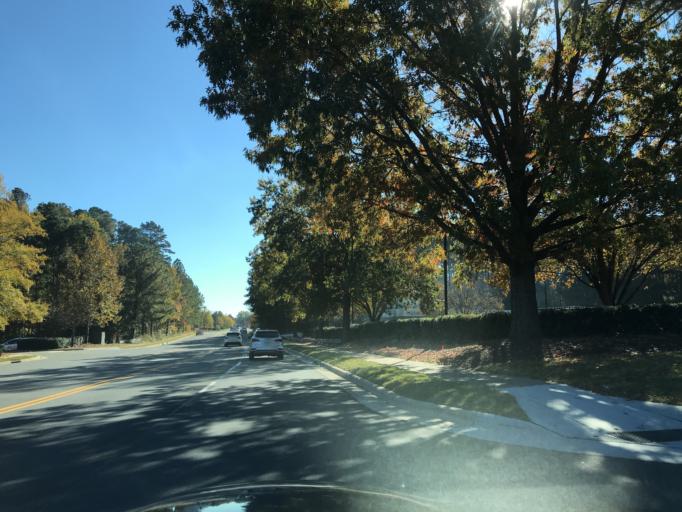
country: US
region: North Carolina
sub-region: Wake County
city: Raleigh
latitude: 35.8475
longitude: -78.6018
